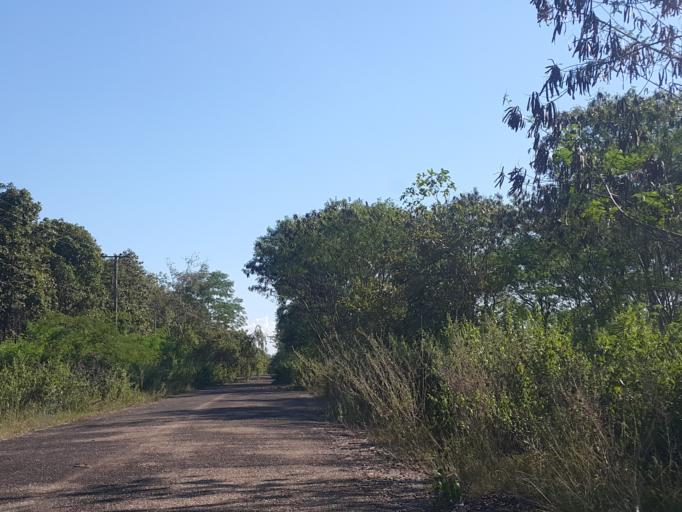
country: TH
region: Chiang Mai
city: San Sai
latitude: 18.9234
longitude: 99.1148
